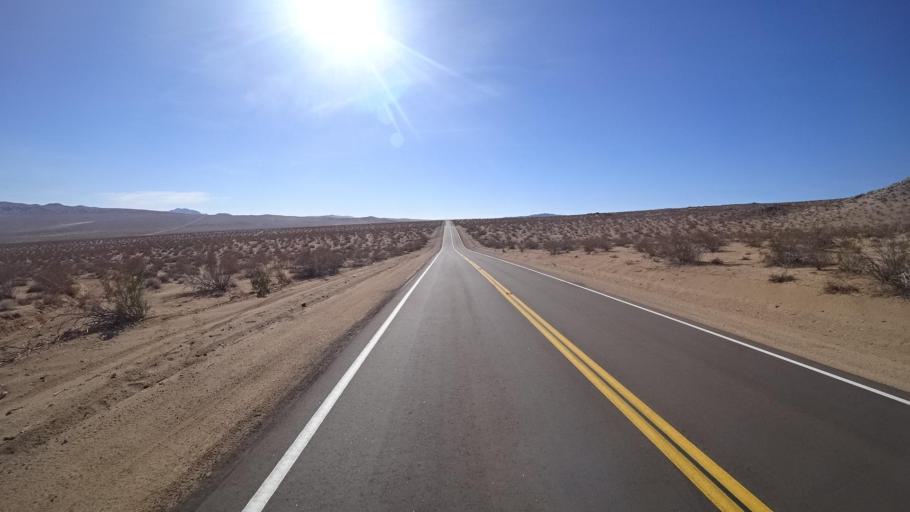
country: US
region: California
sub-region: Kern County
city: Ridgecrest
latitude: 35.5369
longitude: -117.5881
